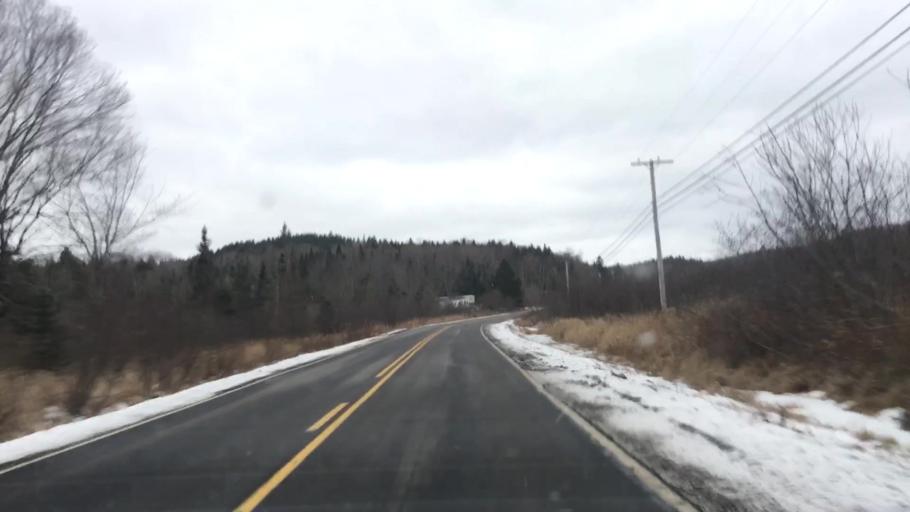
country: US
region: Maine
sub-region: Washington County
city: Machiasport
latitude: 44.7084
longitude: -67.3662
